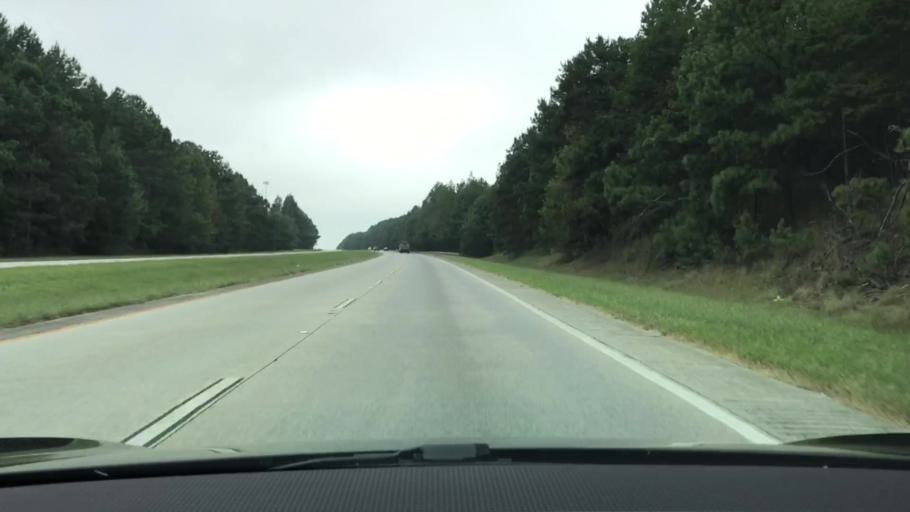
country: US
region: Georgia
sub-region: Barrow County
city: Statham
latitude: 33.9606
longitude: -83.6427
